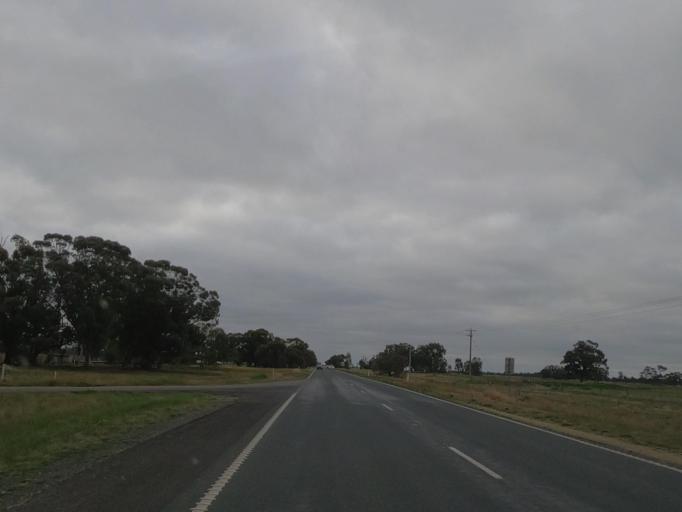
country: AU
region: Victoria
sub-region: Greater Bendigo
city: Long Gully
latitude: -36.3125
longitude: 143.9749
